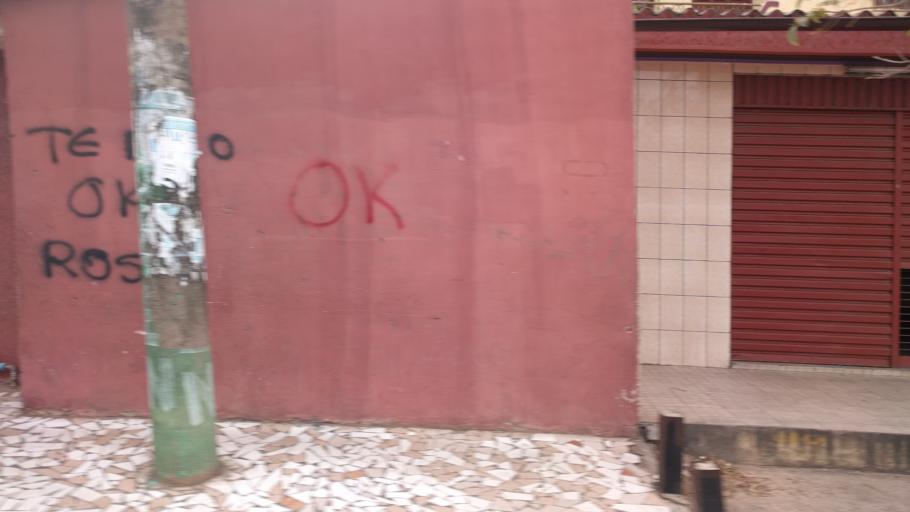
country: BO
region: Santa Cruz
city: Santa Cruz de la Sierra
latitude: -17.7783
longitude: -63.2053
